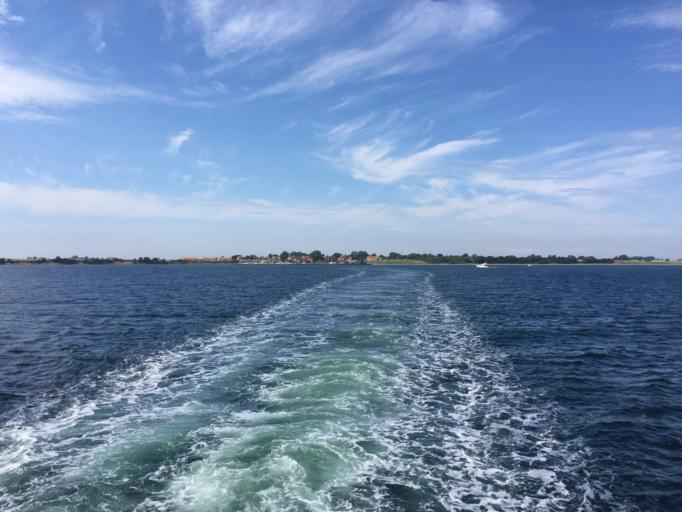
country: DK
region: Zealand
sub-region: Slagelse Kommune
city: Skaelskor
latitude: 55.2114
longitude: 11.2127
